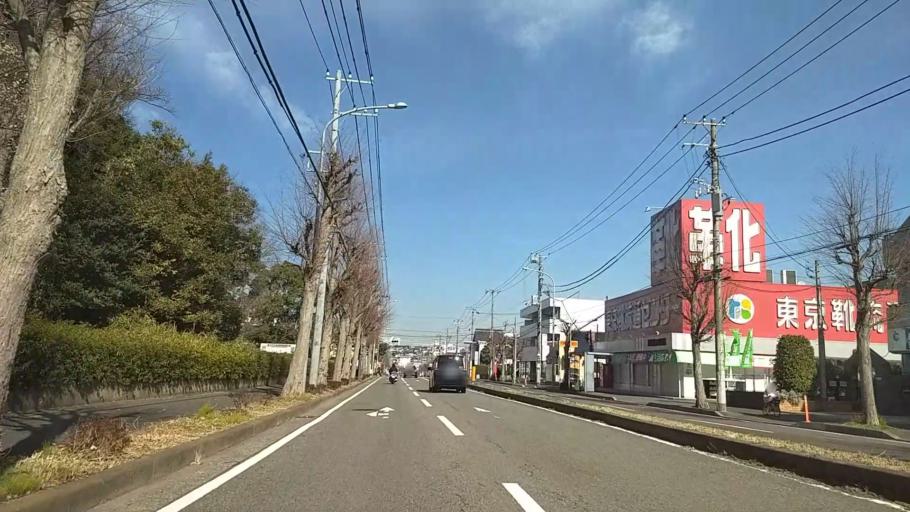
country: JP
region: Kanagawa
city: Kamakura
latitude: 35.3763
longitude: 139.5813
